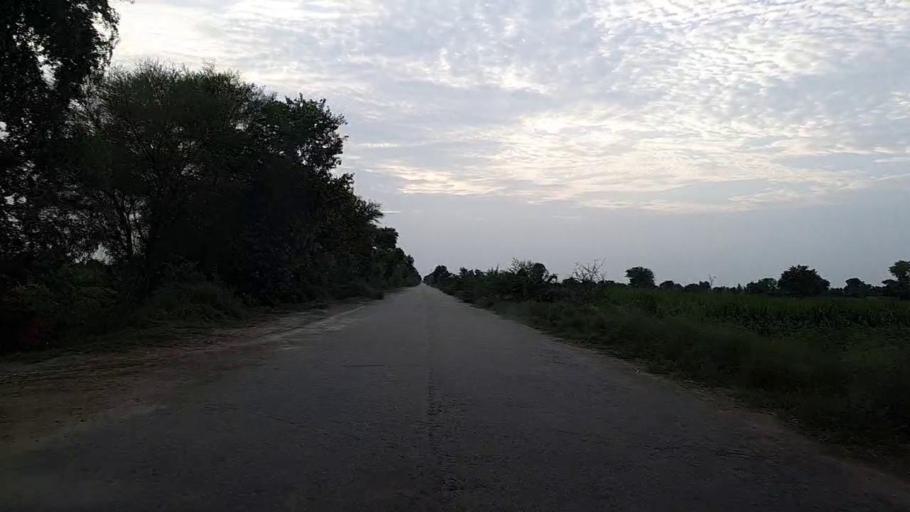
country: PK
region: Sindh
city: Pad Idan
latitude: 26.8033
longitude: 68.2179
